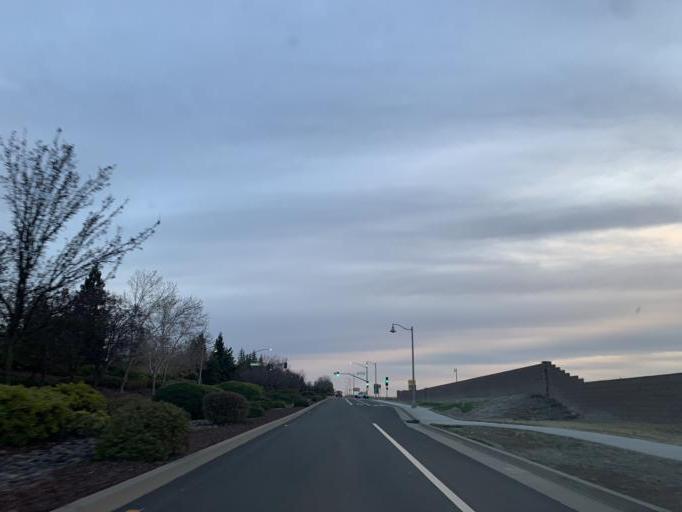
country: US
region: California
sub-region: Placer County
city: Lincoln
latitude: 38.8612
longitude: -121.2846
